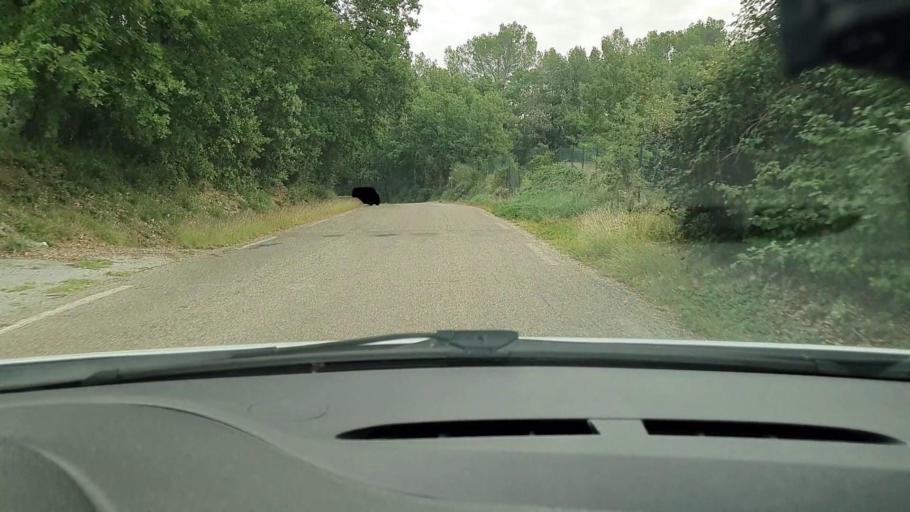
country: FR
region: Languedoc-Roussillon
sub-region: Departement du Gard
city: Saint-Chaptes
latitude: 44.0448
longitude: 4.3030
